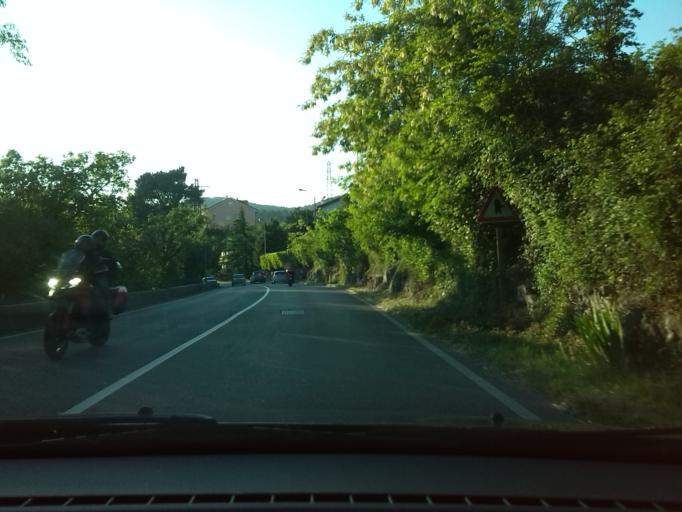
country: IT
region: Friuli Venezia Giulia
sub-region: Provincia di Trieste
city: Sistiana-Visogliano
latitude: 45.7728
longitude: 13.6351
